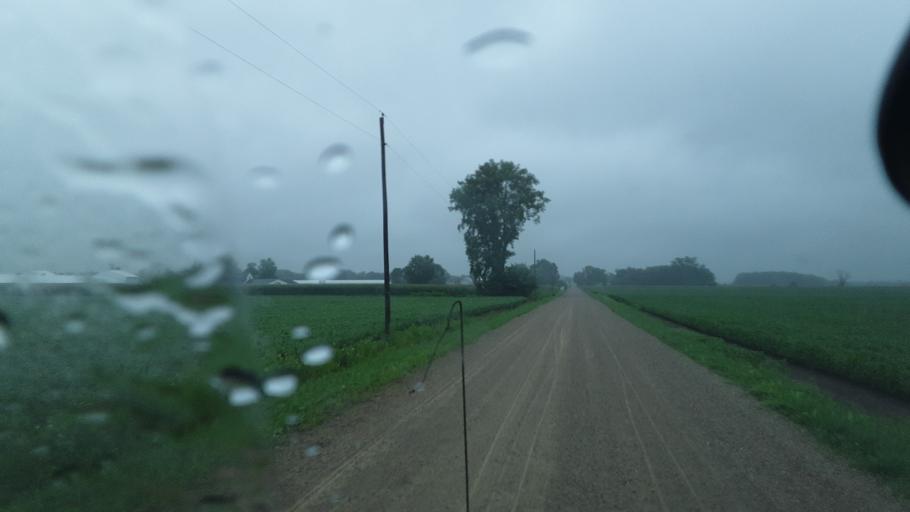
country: US
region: Indiana
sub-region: Adams County
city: Berne
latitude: 40.6346
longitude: -85.0099
